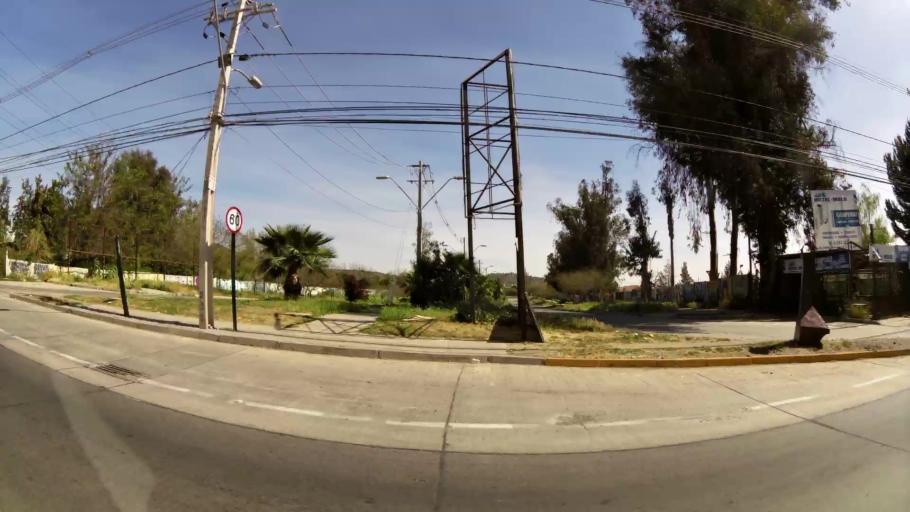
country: CL
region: Santiago Metropolitan
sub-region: Provincia de Cordillera
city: Puente Alto
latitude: -33.5930
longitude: -70.5391
